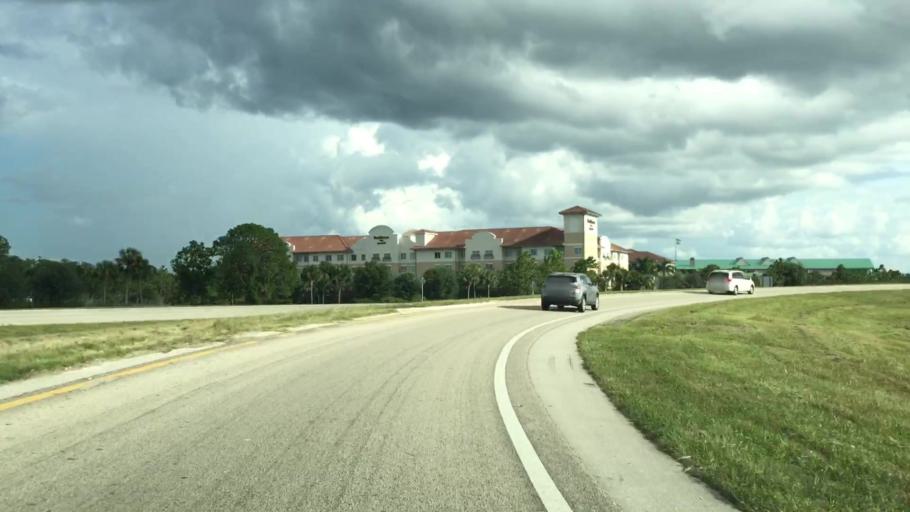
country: US
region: Florida
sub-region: Lee County
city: Three Oaks
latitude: 26.4923
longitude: -81.7923
